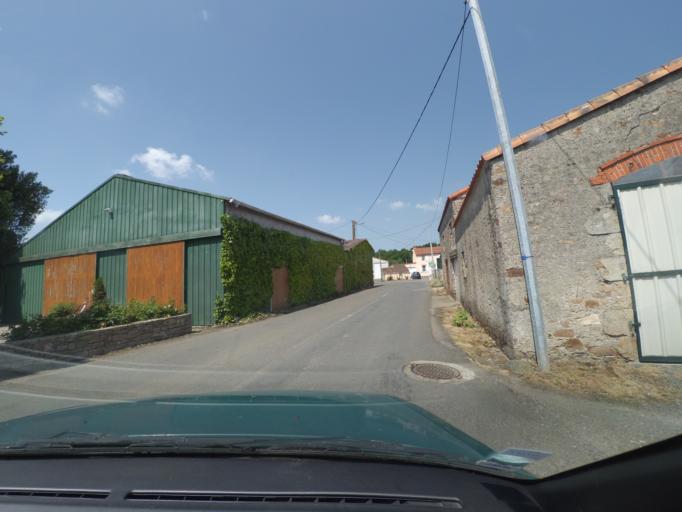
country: FR
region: Pays de la Loire
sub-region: Departement de la Loire-Atlantique
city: Gorges
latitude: 47.1171
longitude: -1.2884
